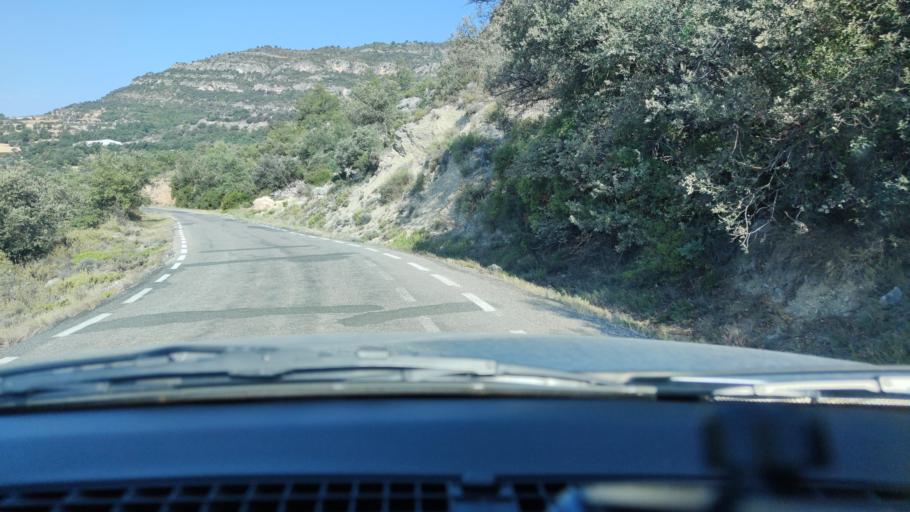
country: ES
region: Catalonia
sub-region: Provincia de Lleida
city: Llimiana
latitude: 42.0846
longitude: 0.8518
